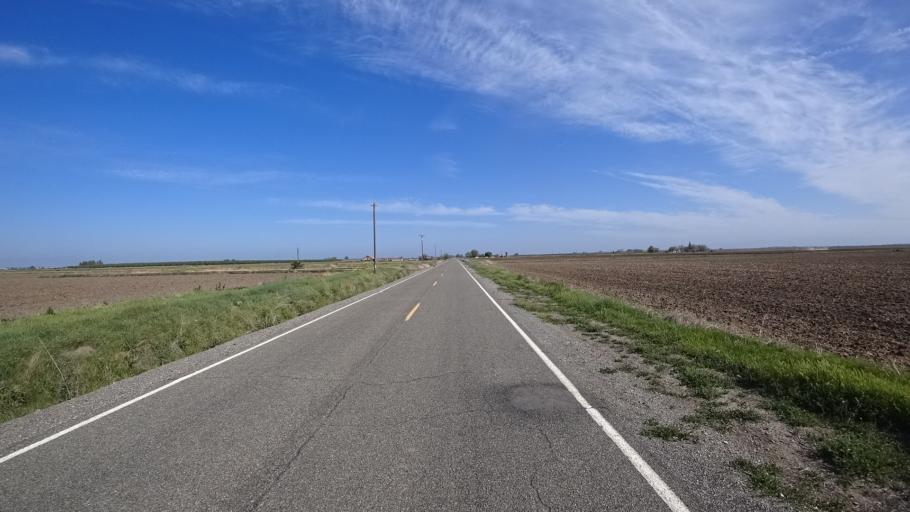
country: US
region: California
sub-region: Glenn County
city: Hamilton City
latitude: 39.6038
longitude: -122.0369
